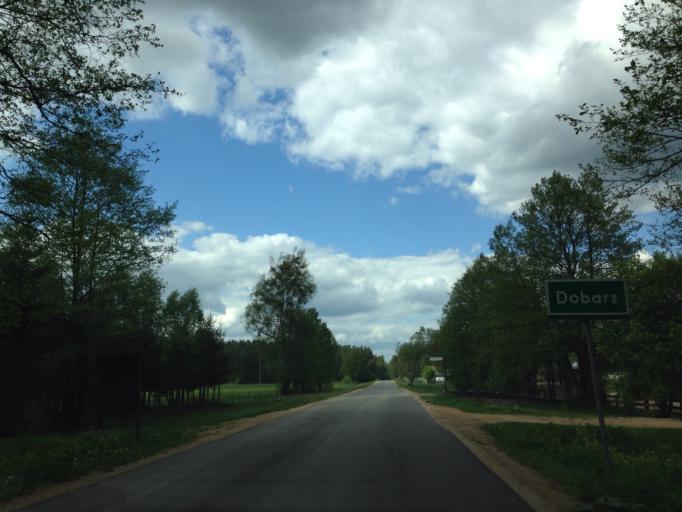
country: PL
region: Podlasie
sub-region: Powiat grajewski
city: Radzilow
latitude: 53.3683
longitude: 22.5925
